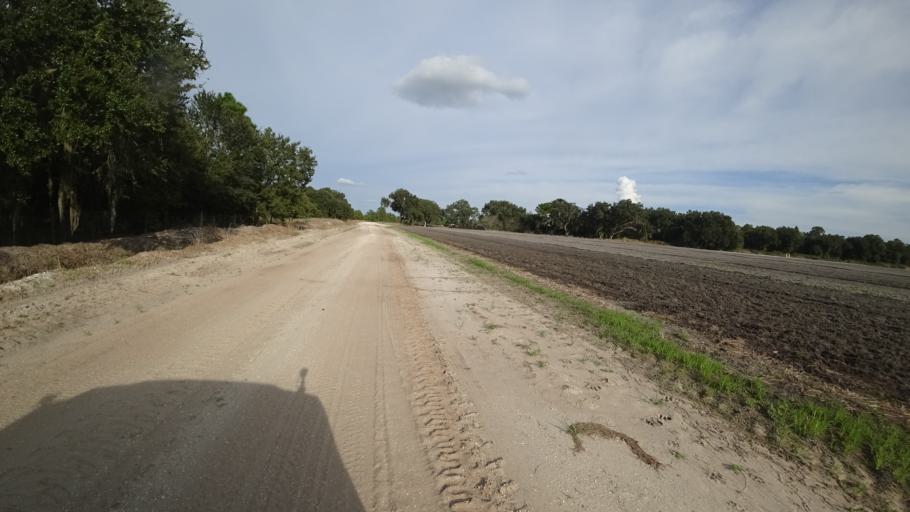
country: US
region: Florida
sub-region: Hillsborough County
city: Wimauma
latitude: 27.5655
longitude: -82.0923
